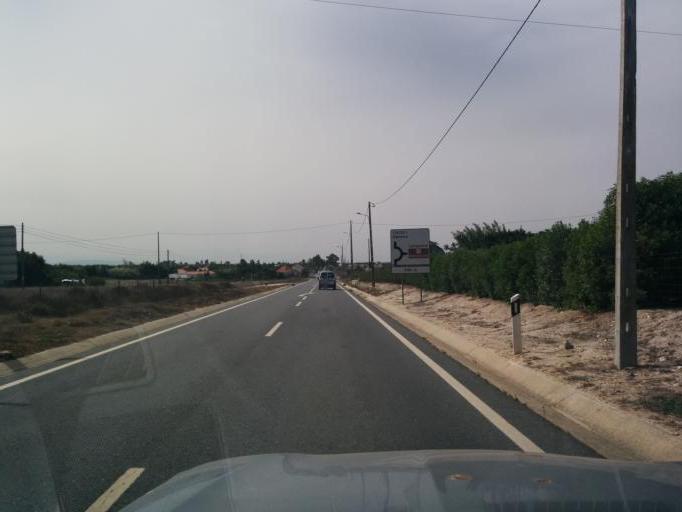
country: PT
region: Beja
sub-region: Odemira
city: Vila Nova de Milfontes
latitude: 37.6588
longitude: -8.7596
